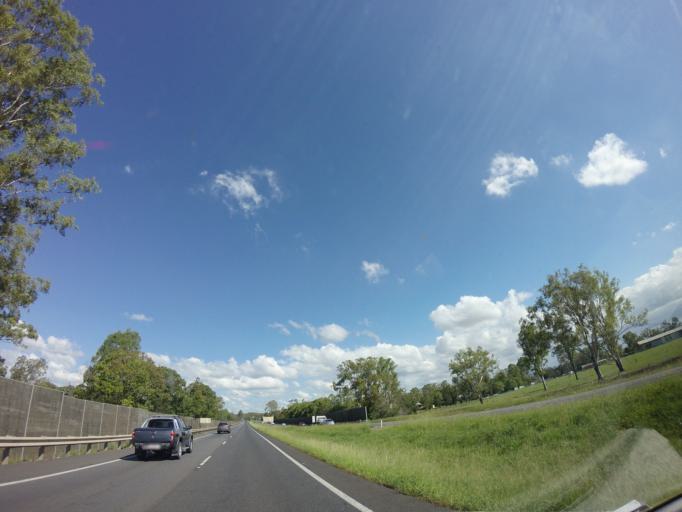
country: AU
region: Queensland
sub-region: Ipswich
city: North Booval
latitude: -27.5785
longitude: 152.8064
